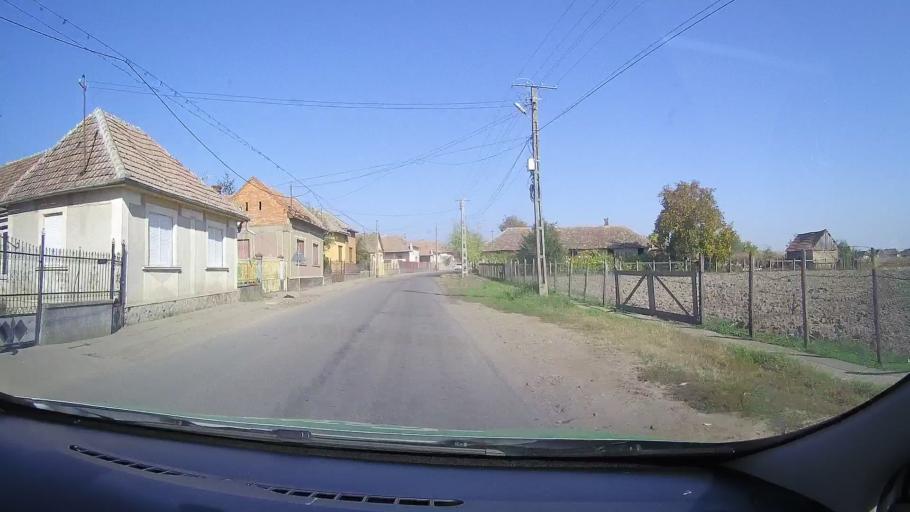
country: RO
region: Satu Mare
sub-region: Comuna Ciumesti
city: Ciumesti
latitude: 47.6568
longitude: 22.3337
